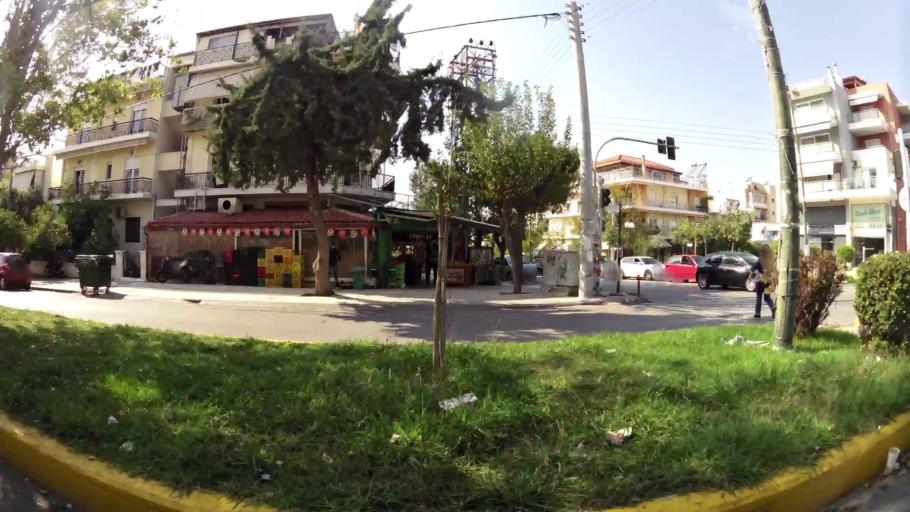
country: GR
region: Attica
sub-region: Nomarchia Athinas
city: Agios Dimitrios
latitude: 37.9286
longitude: 23.7475
